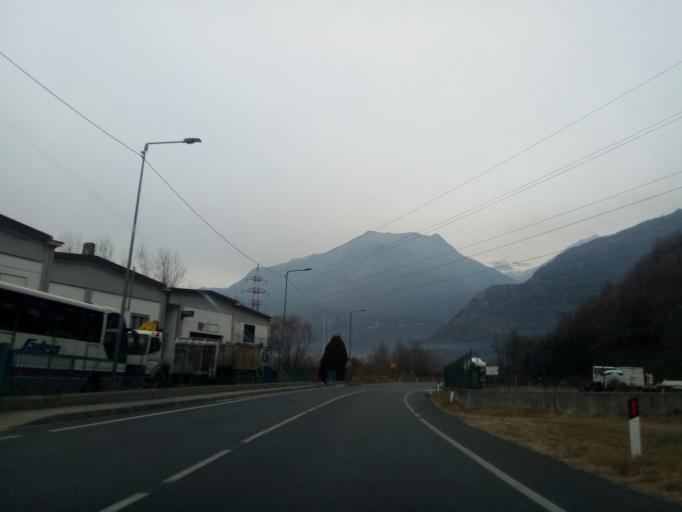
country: IT
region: Piedmont
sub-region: Provincia di Torino
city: Quincinetto
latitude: 45.5728
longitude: 7.8105
